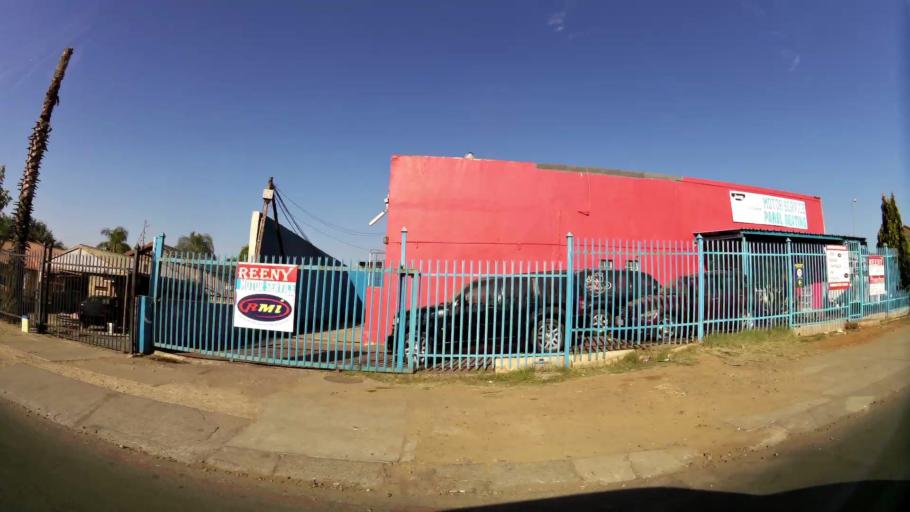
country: ZA
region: Gauteng
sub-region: City of Tshwane Metropolitan Municipality
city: Pretoria
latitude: -25.7193
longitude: 28.1532
